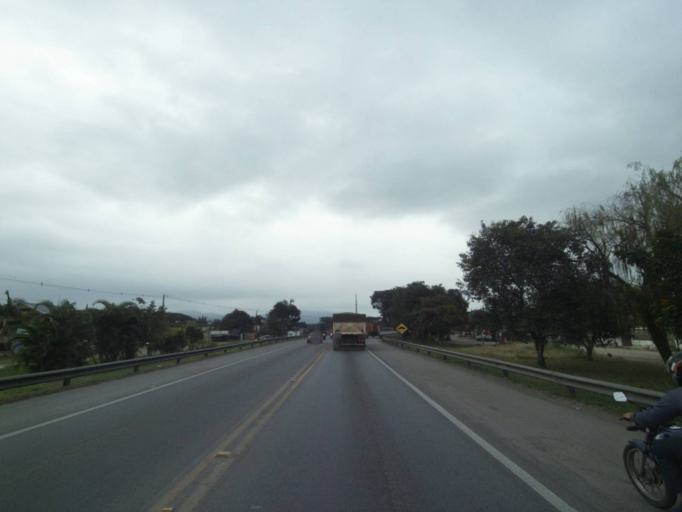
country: BR
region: Parana
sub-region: Paranagua
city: Paranagua
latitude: -25.5244
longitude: -48.5475
